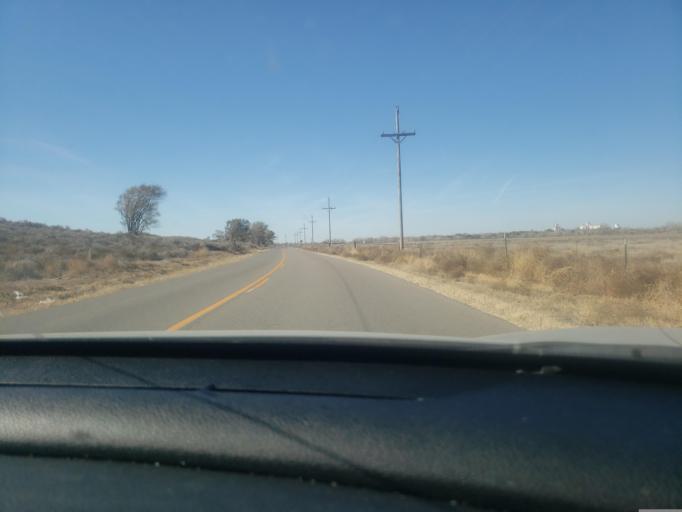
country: US
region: Kansas
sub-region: Finney County
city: Garden City
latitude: 37.9508
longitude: -100.8549
